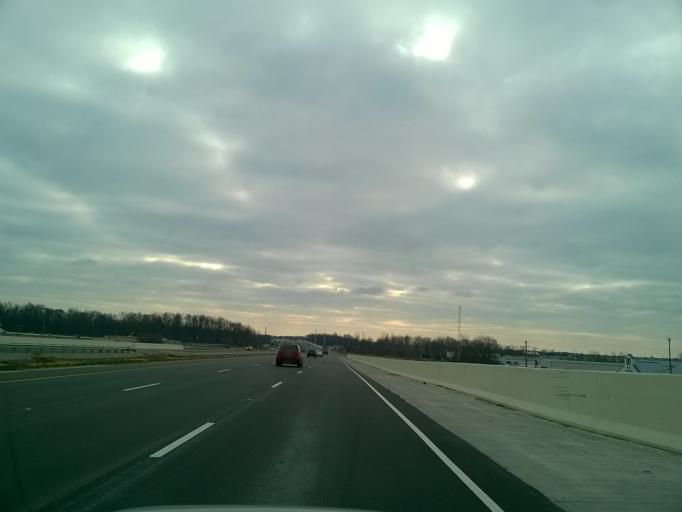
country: US
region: Indiana
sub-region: Hamilton County
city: Westfield
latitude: 40.0398
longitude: -86.1362
